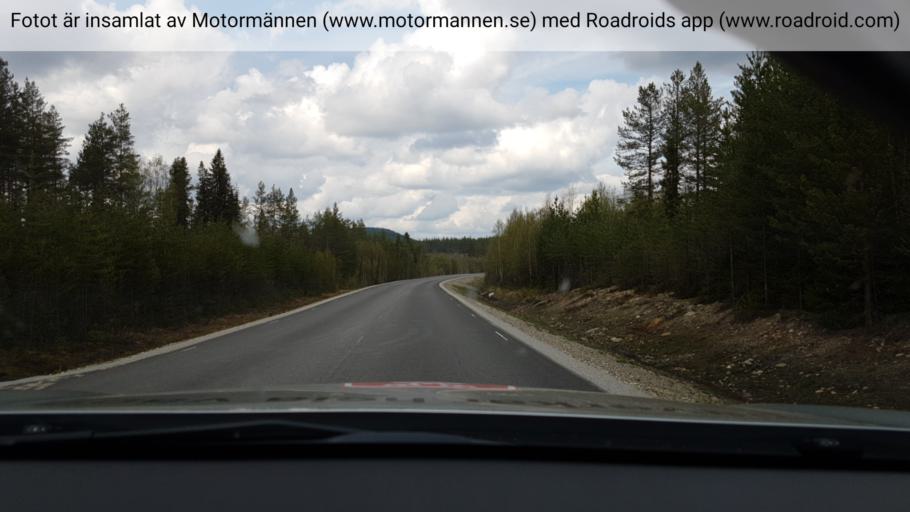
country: SE
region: Vaesterbotten
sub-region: Lycksele Kommun
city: Lycksele
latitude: 64.0090
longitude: 18.4600
